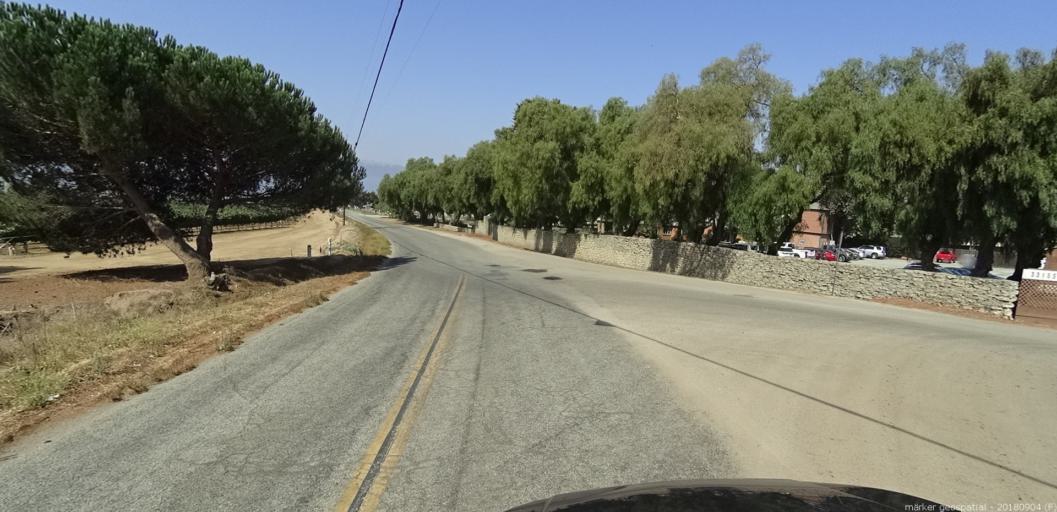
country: US
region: California
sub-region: Monterey County
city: Gonzales
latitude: 36.5040
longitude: -121.3832
